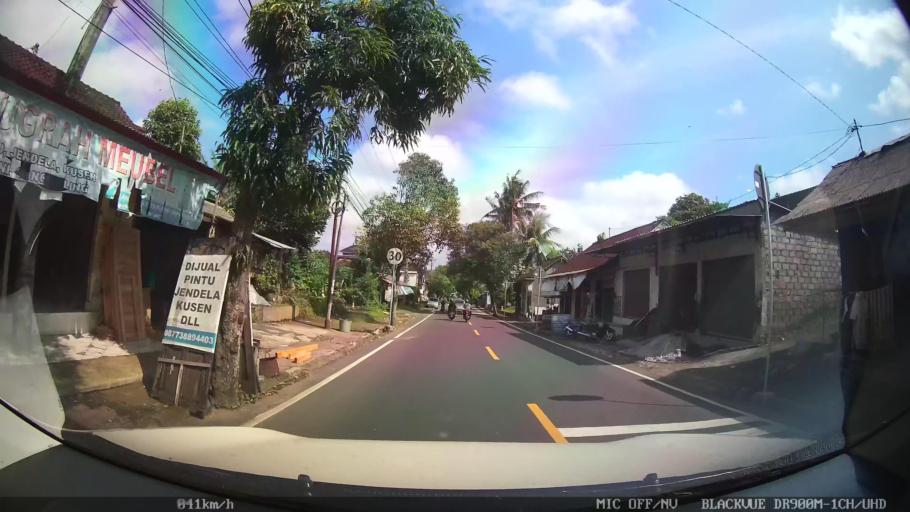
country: ID
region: Bali
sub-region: Kabupaten Gianyar
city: Ubud
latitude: -8.5077
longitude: 115.2930
